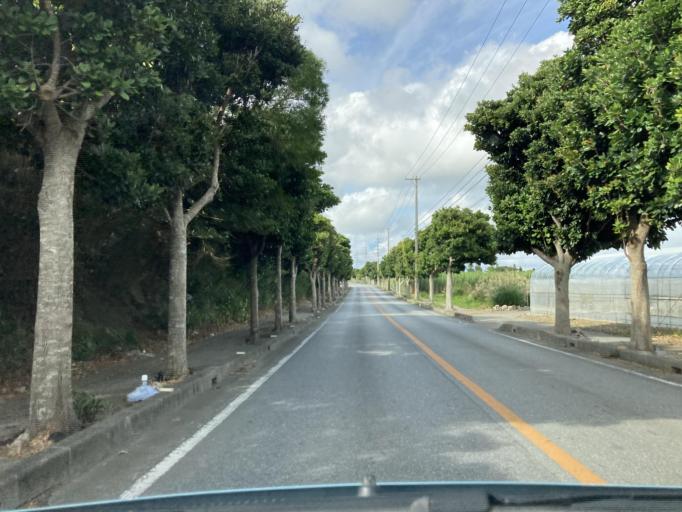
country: JP
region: Okinawa
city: Itoman
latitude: 26.1168
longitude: 127.7165
